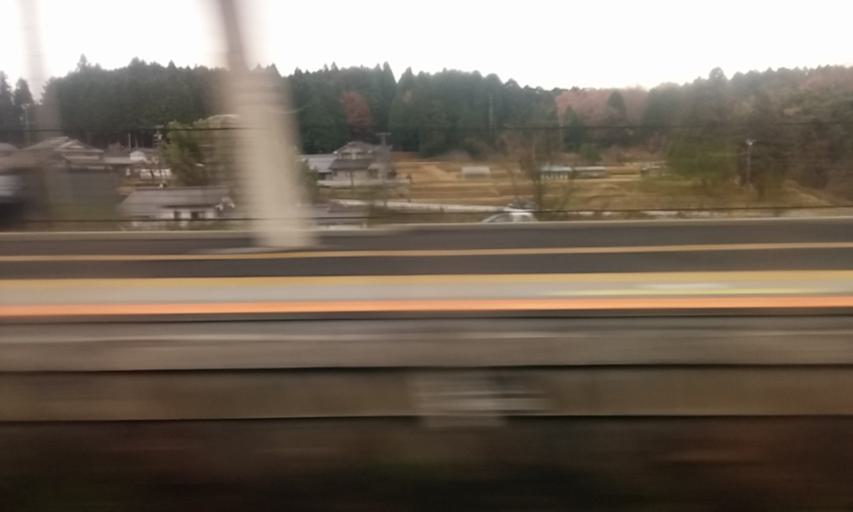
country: JP
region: Gifu
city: Mizunami
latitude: 35.4377
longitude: 137.3538
